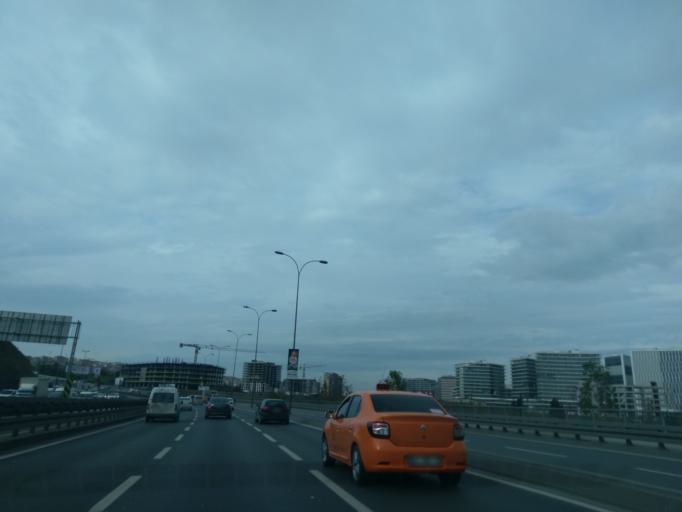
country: TR
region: Istanbul
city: Bahcelievler
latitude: 40.9971
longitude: 28.8136
